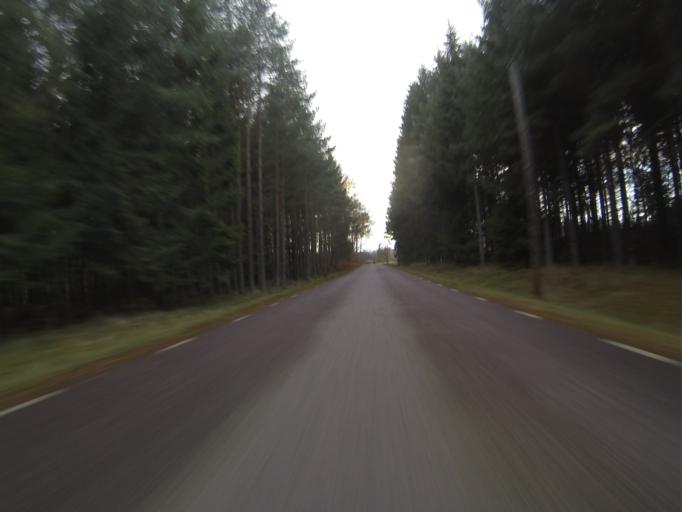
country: SE
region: Skane
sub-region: Lunds Kommun
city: Genarp
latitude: 55.5813
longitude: 13.4051
